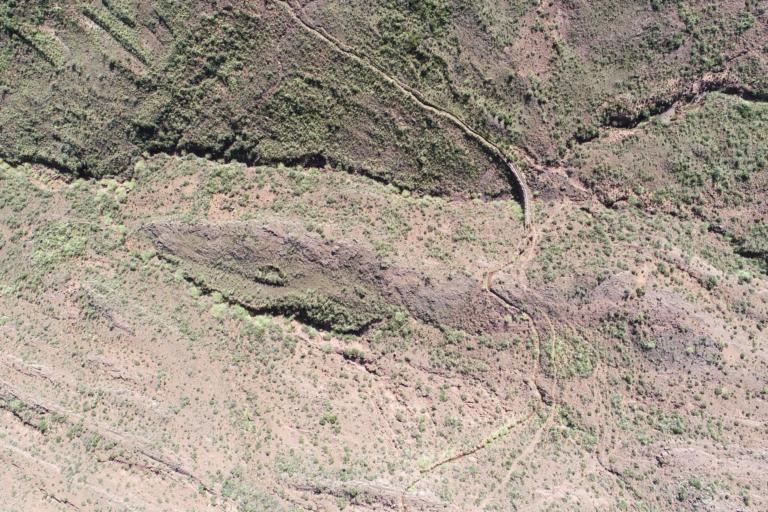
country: BO
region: La Paz
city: Tiahuanaco
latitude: -16.6054
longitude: -68.7574
